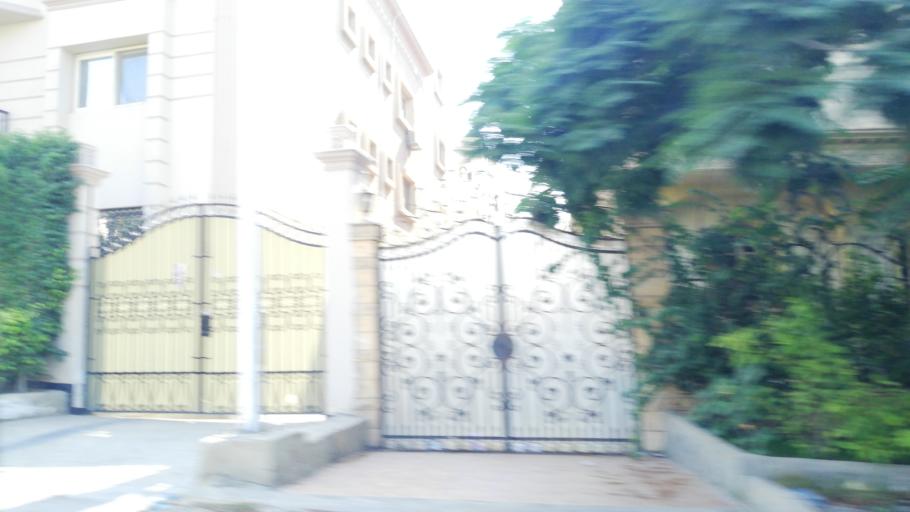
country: EG
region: Muhafazat al Qahirah
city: Cairo
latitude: 30.0155
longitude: 31.4210
